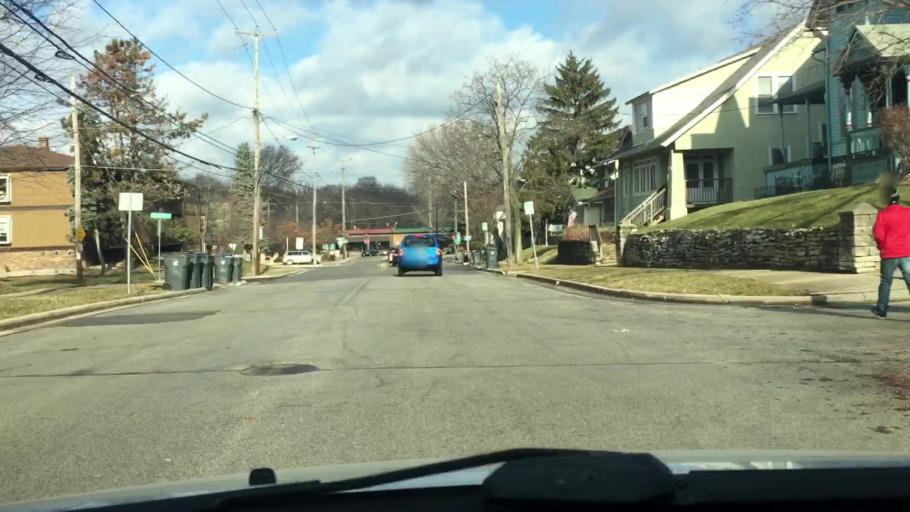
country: US
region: Wisconsin
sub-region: Waukesha County
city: Waukesha
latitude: 43.0087
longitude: -88.2365
